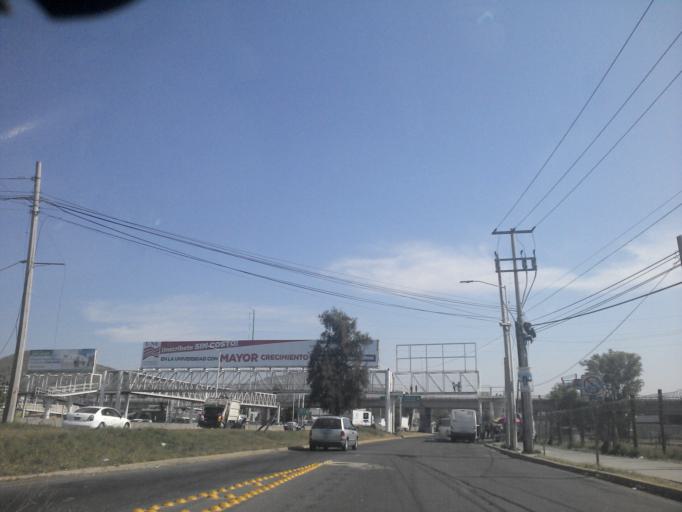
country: MX
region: Jalisco
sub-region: San Pedro Tlaquepaque
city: Paseo del Prado
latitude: 20.6072
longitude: -103.4032
